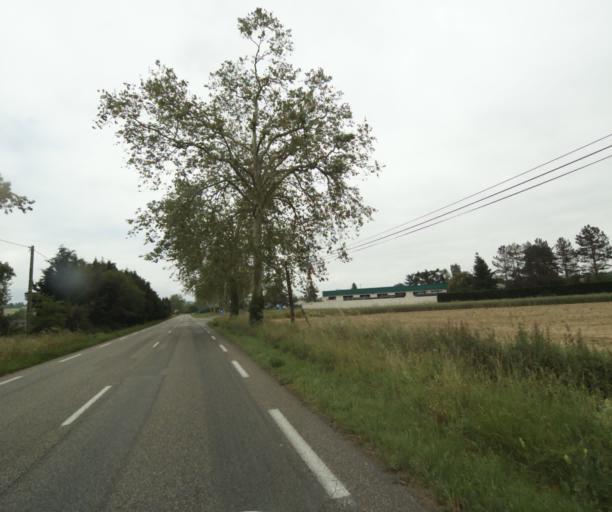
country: FR
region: Midi-Pyrenees
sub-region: Departement du Tarn-et-Garonne
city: Saint-Nauphary
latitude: 43.9750
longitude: 1.4106
